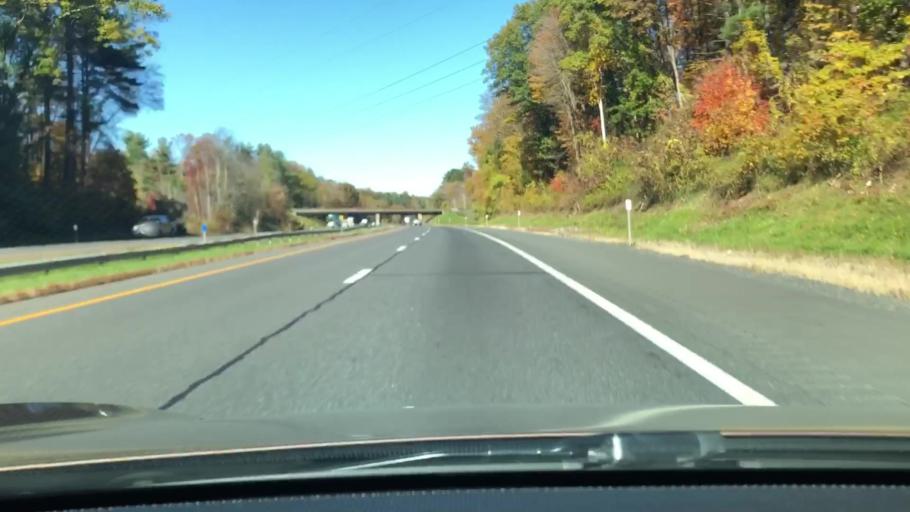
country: US
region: New York
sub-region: Ulster County
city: Rosendale Village
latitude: 41.8657
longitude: -74.0571
